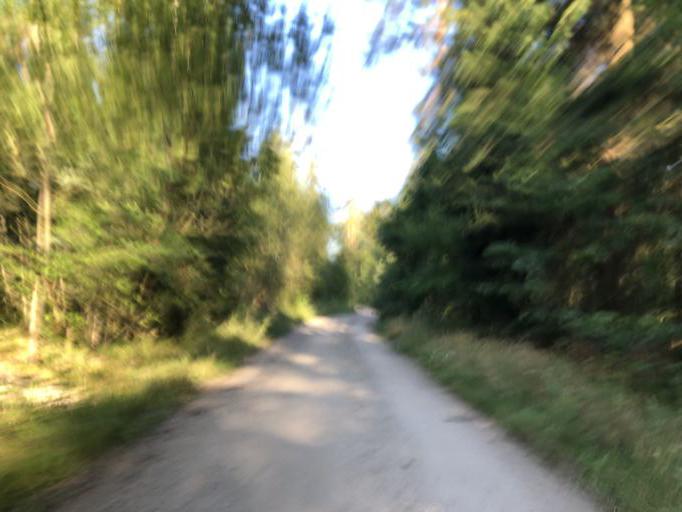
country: DE
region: Bavaria
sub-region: Regierungsbezirk Mittelfranken
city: Buckenhof
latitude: 49.5387
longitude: 11.0390
